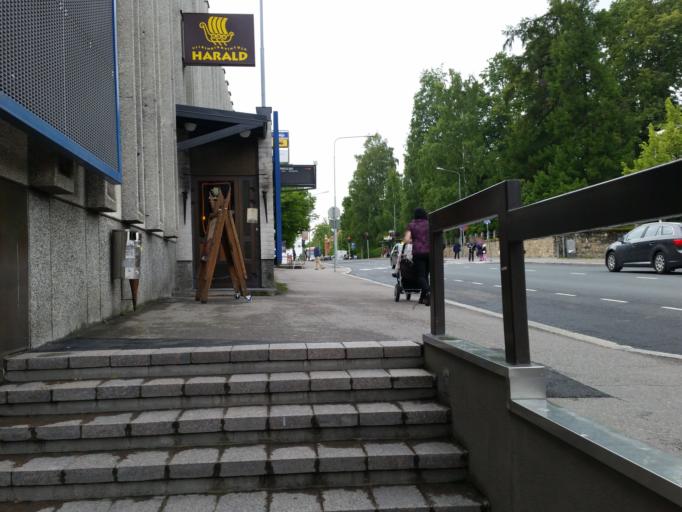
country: FI
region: Northern Savo
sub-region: Kuopio
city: Kuopio
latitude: 62.8931
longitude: 27.6765
